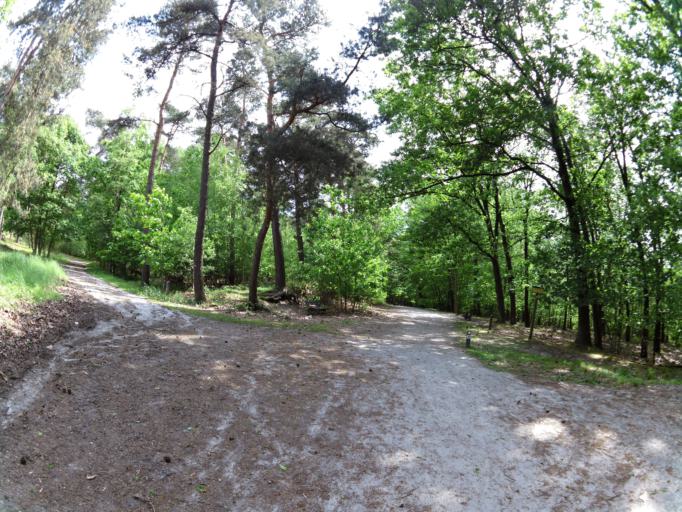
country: NL
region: Limburg
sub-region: Gemeente Brunssum
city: Brunssum
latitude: 50.9326
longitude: 5.9985
